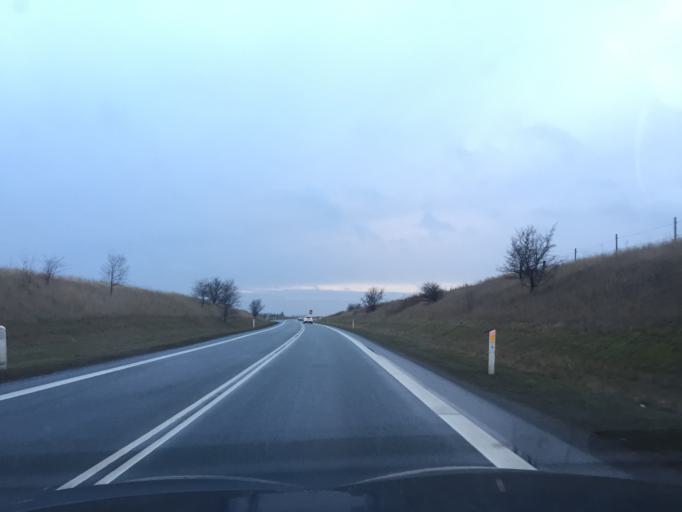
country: DK
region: Zealand
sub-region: Slagelse Kommune
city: Slagelse
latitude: 55.3650
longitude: 11.3306
